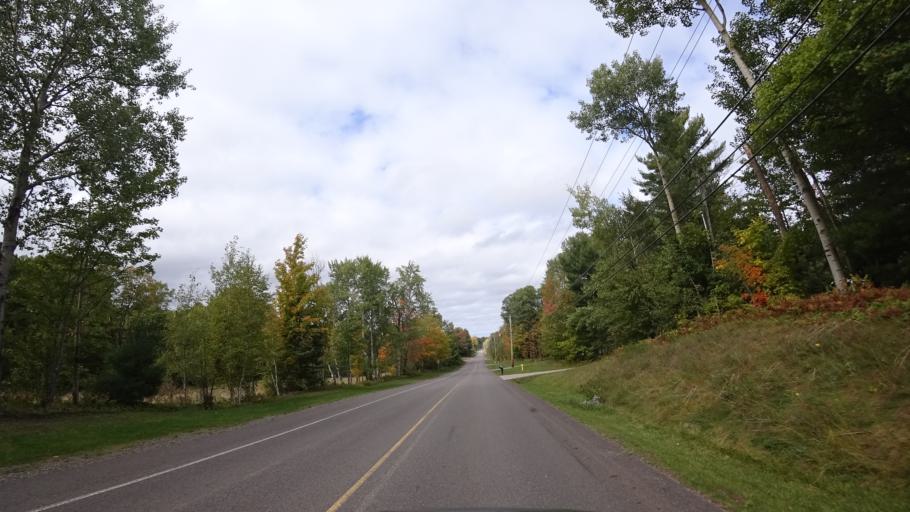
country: US
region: Michigan
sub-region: Marquette County
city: Trowbridge Park
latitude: 46.5411
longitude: -87.4374
